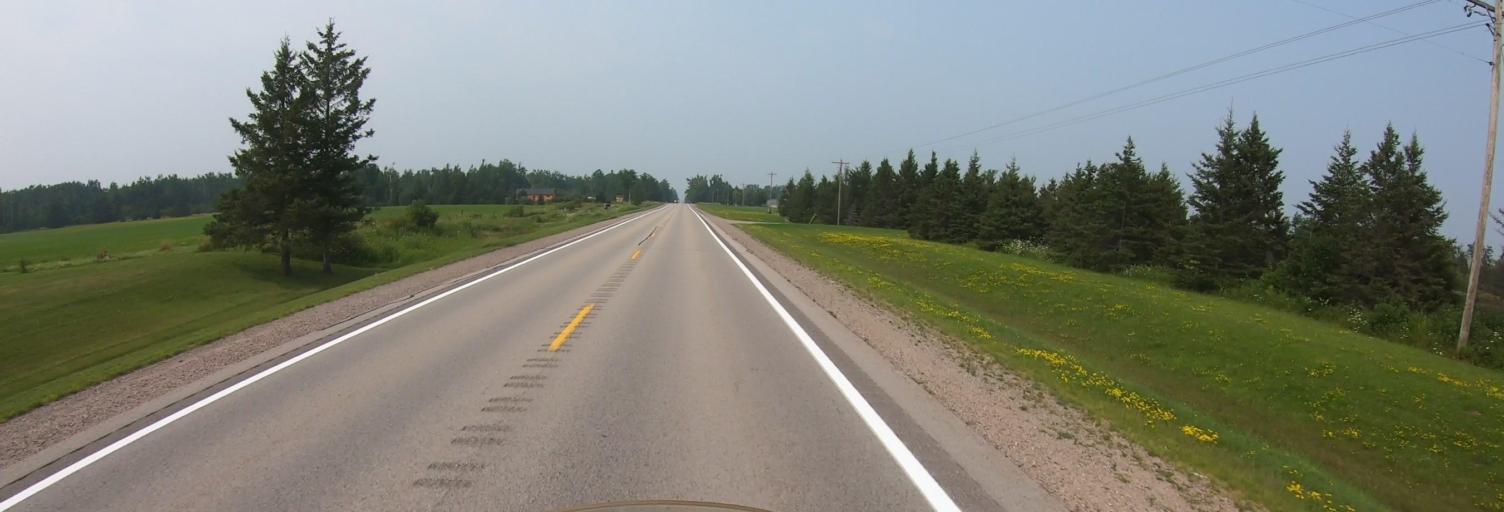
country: US
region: Michigan
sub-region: Chippewa County
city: Sault Ste. Marie
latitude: 46.2349
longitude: -84.3633
